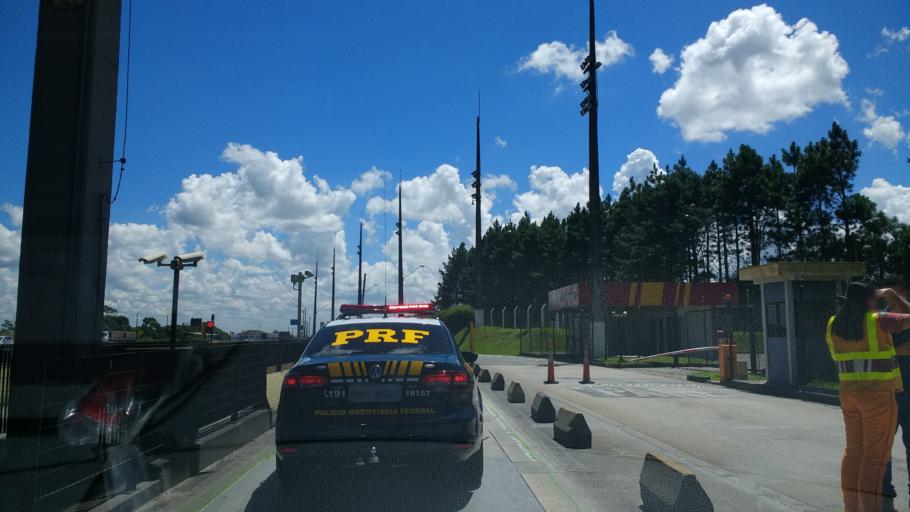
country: BR
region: Parana
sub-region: Campo Largo
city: Campo Largo
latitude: -25.4712
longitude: -49.6620
